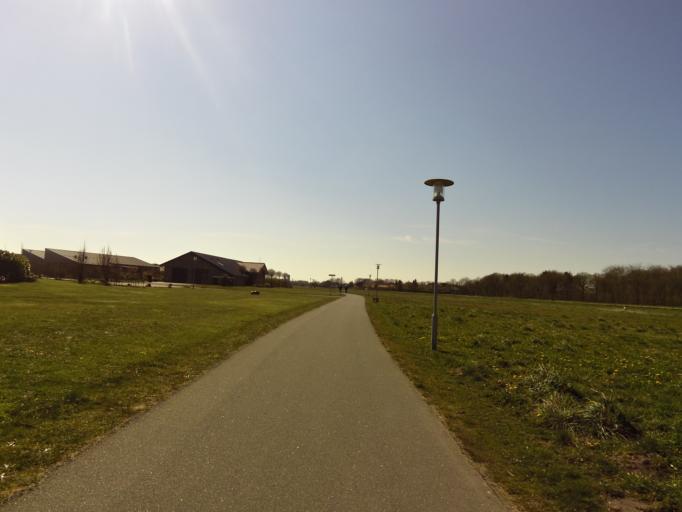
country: DK
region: South Denmark
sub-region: Esbjerg Kommune
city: Ribe
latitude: 55.3407
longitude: 8.7937
